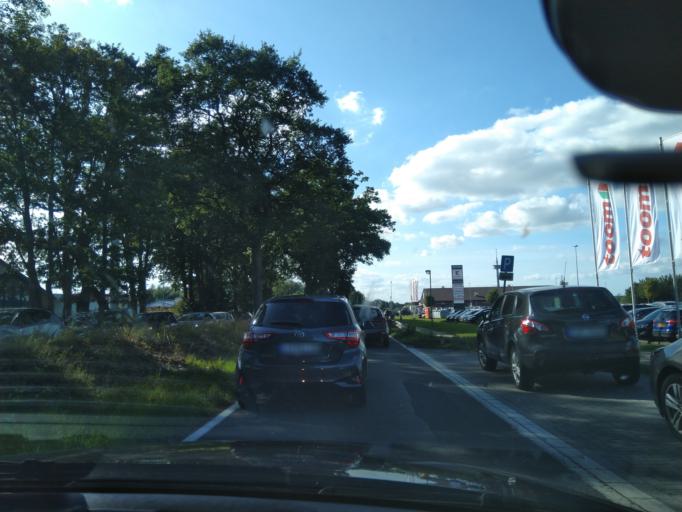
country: DE
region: Lower Saxony
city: Leer
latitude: 53.2593
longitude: 7.4569
